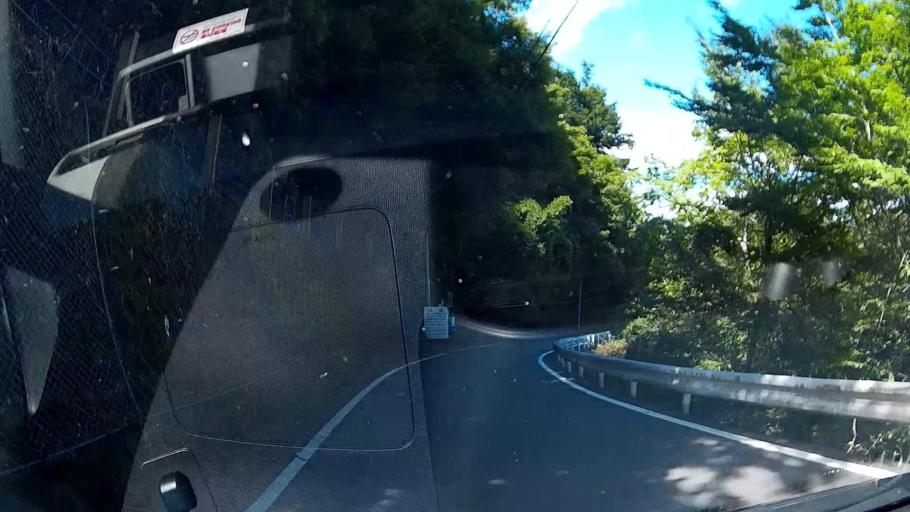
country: JP
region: Shizuoka
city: Shizuoka-shi
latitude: 35.1992
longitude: 138.2367
